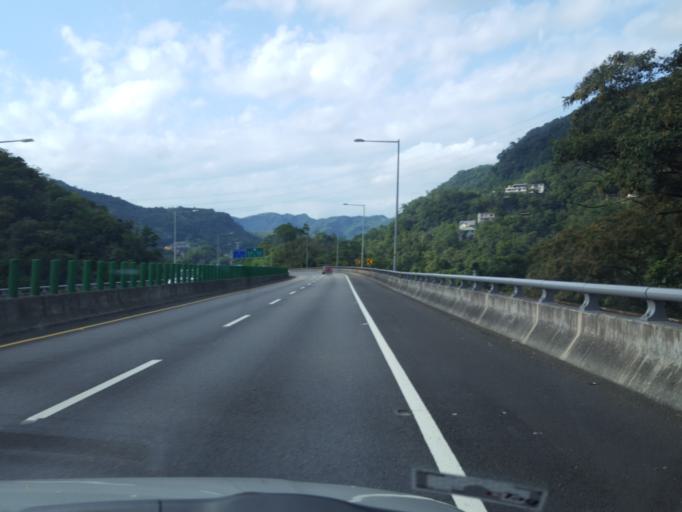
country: TW
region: Taipei
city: Taipei
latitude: 24.9877
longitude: 121.6594
